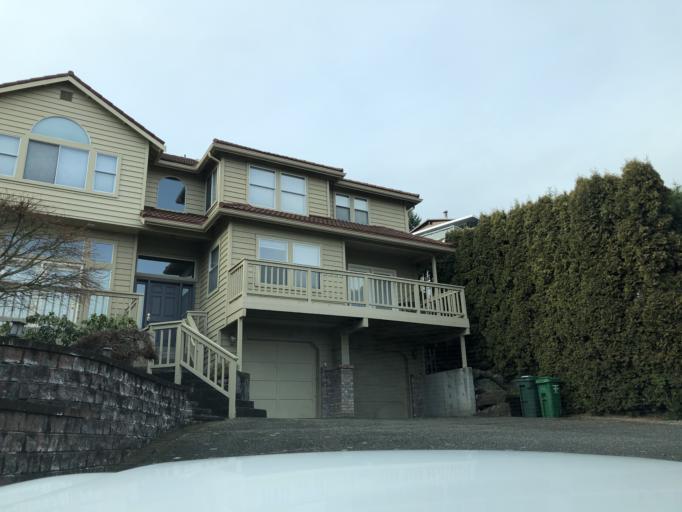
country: US
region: Washington
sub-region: King County
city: Lake Forest Park
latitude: 47.7119
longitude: -122.2797
